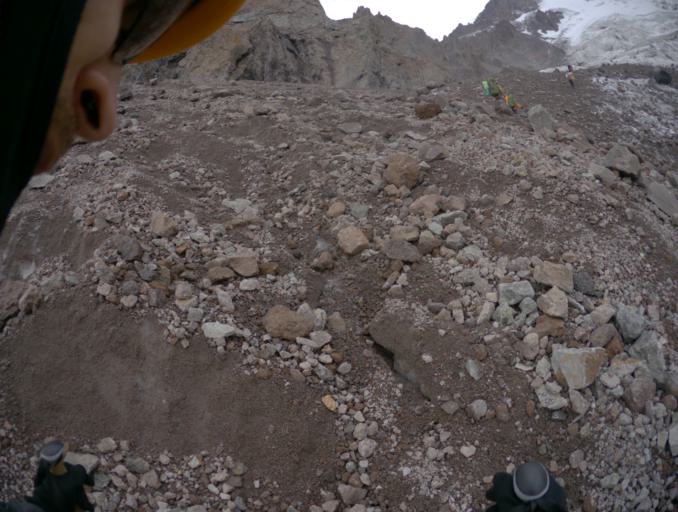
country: RU
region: Kabardino-Balkariya
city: Terskol
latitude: 43.3811
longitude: 42.3968
